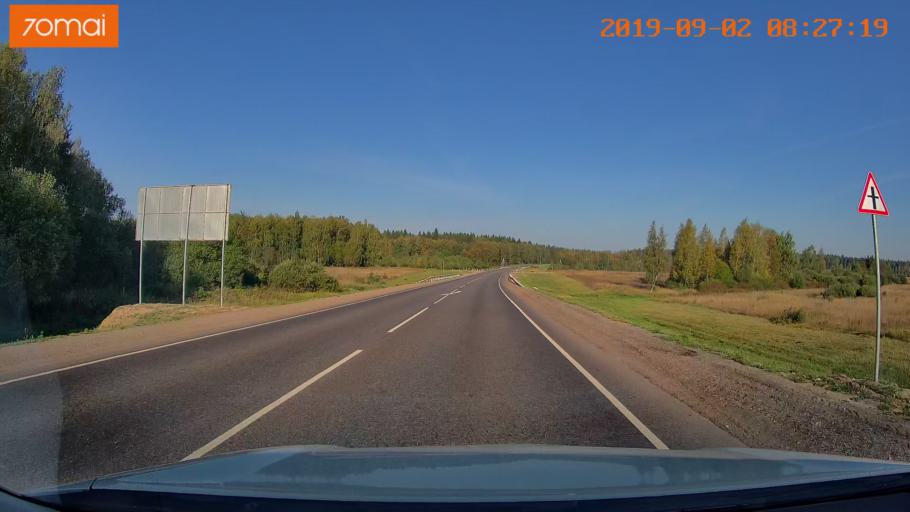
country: RU
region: Kaluga
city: Maloyaroslavets
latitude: 54.9810
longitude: 36.4196
